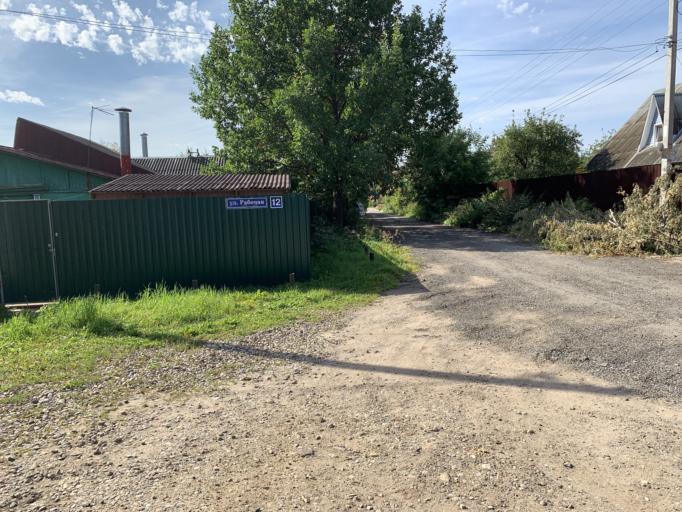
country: RU
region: Moskovskaya
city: Lesnyye Polyany
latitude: 55.9831
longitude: 37.8475
